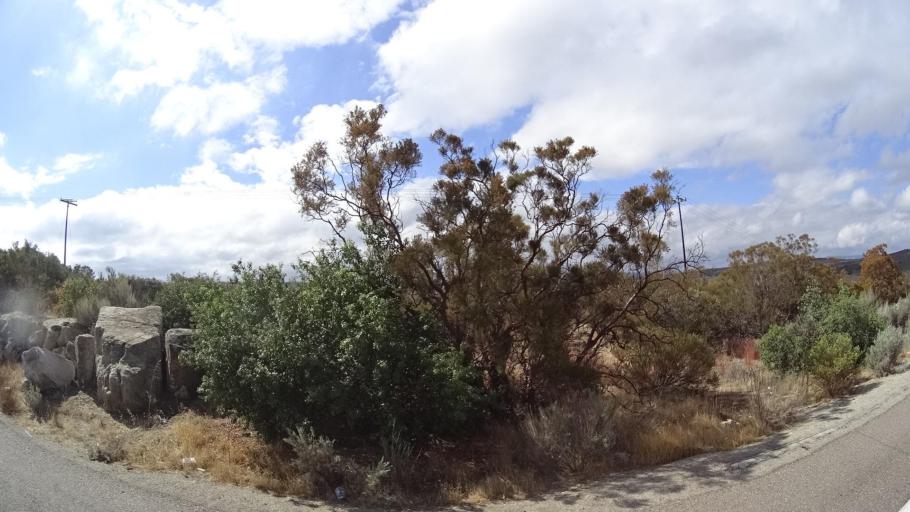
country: US
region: California
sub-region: San Diego County
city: Campo
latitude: 32.6763
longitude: -116.3304
